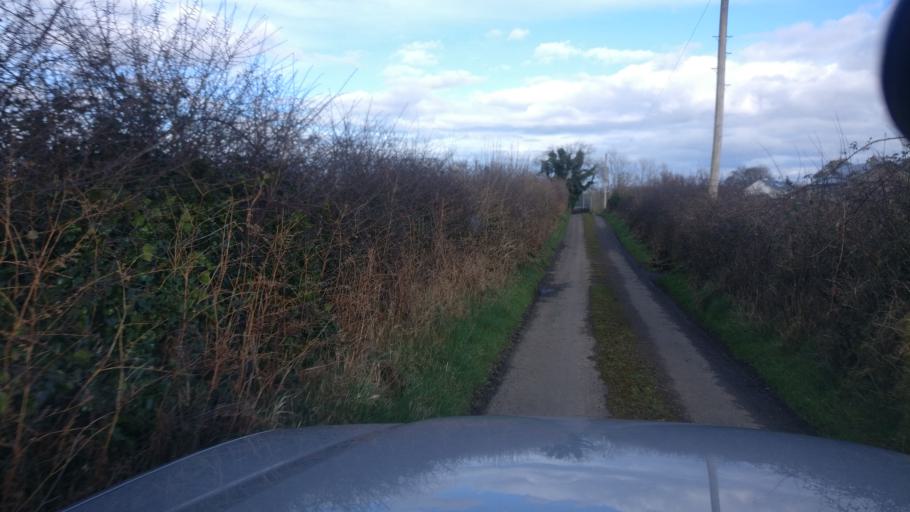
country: IE
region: Connaught
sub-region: County Galway
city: Loughrea
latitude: 53.1827
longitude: -8.4391
